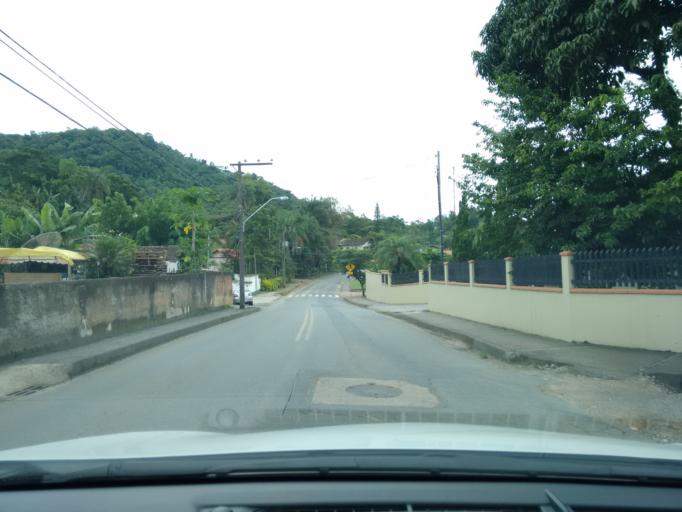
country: BR
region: Santa Catarina
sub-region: Blumenau
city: Blumenau
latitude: -26.8552
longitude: -49.1323
